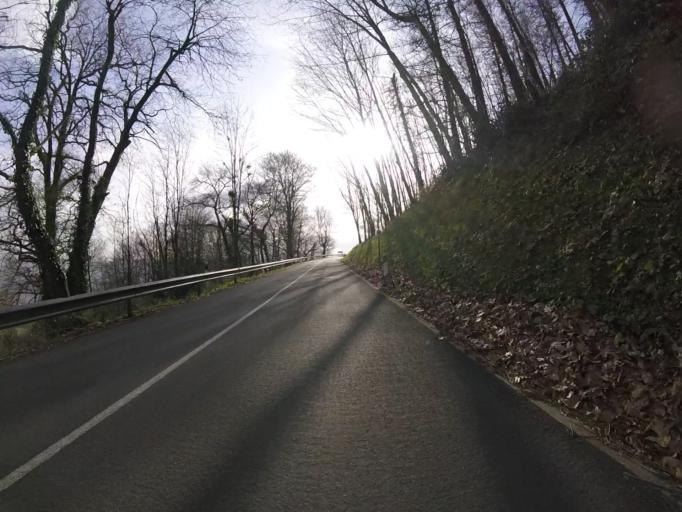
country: ES
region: Basque Country
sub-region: Provincia de Guipuzcoa
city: Asteasu
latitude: 43.2014
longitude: -2.1158
